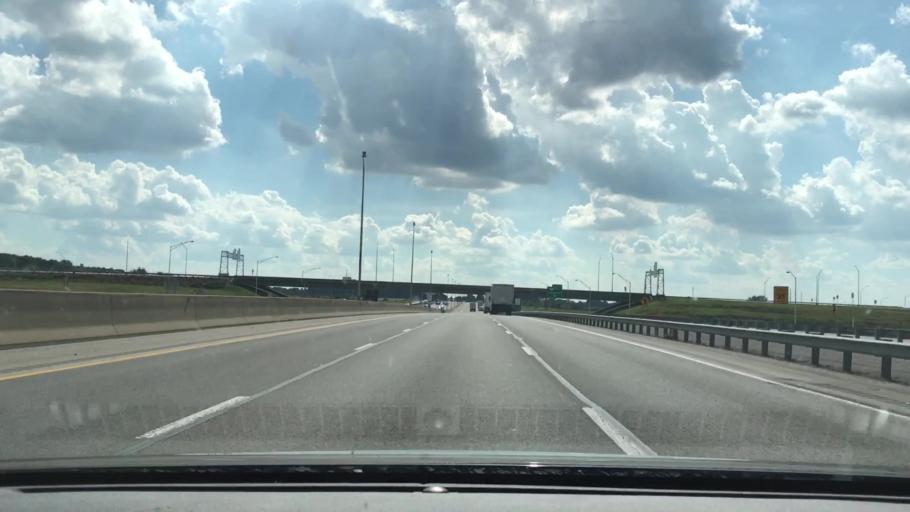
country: US
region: Kentucky
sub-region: Warren County
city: Plano
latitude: 36.9125
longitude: -86.4310
